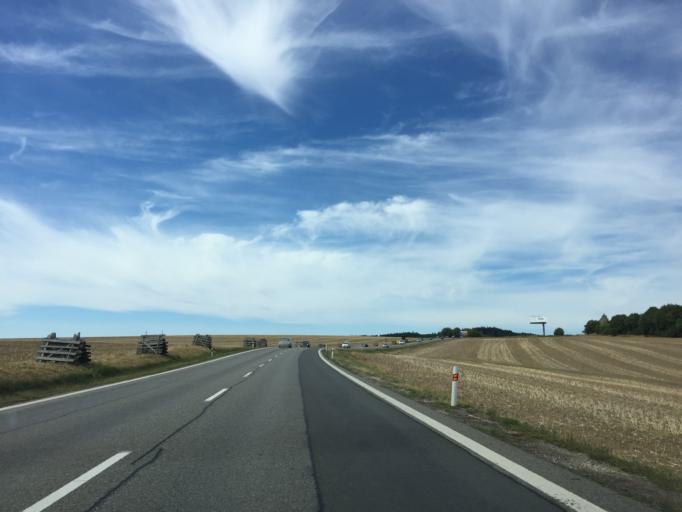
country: CZ
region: Jihocesky
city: Chotoviny
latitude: 49.5583
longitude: 14.6636
